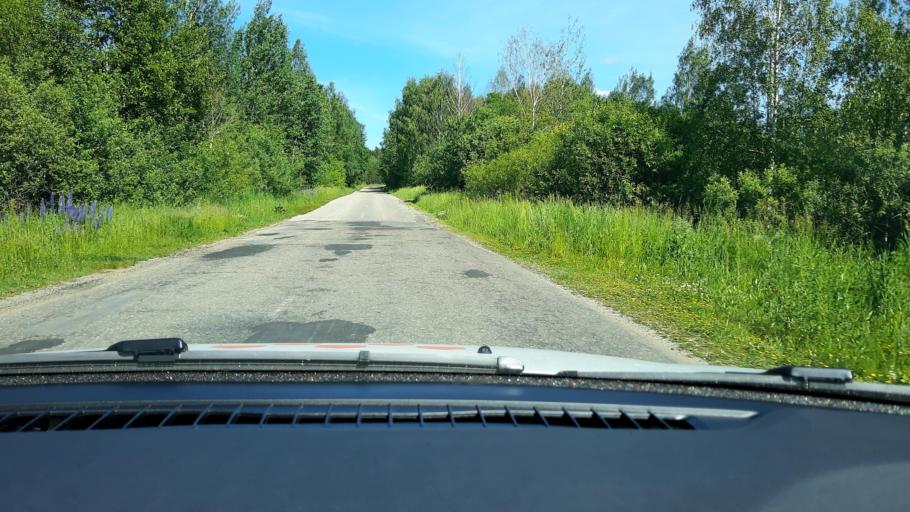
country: RU
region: Nizjnij Novgorod
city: Sitniki
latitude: 56.5248
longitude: 44.1204
